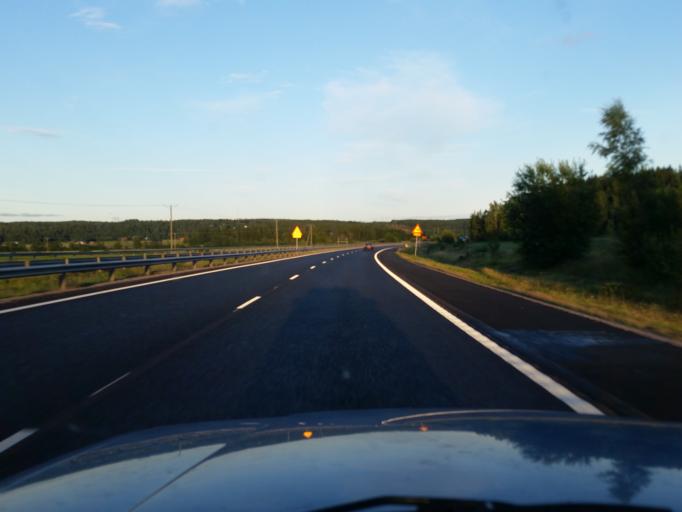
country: FI
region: Varsinais-Suomi
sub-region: Turku
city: Paimio
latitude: 60.4341
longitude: 22.6472
